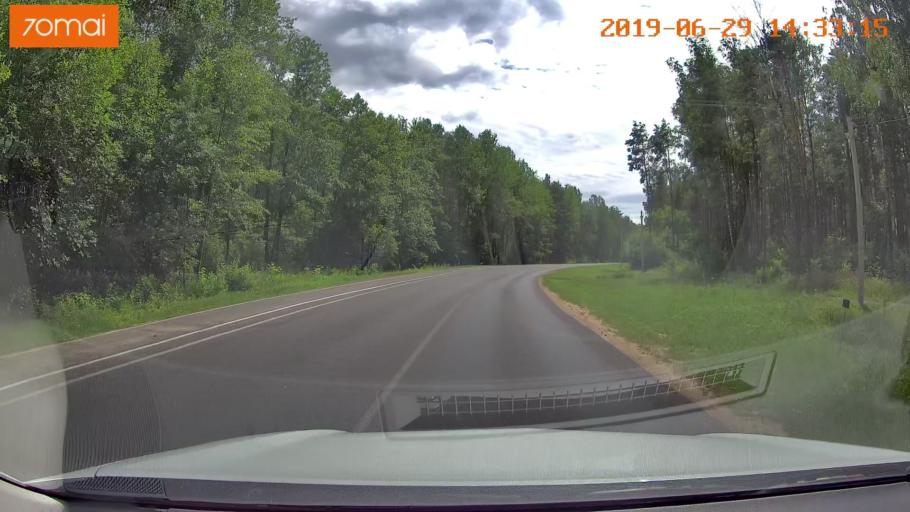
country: BY
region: Minsk
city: Salihorsk
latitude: 52.7798
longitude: 27.5018
